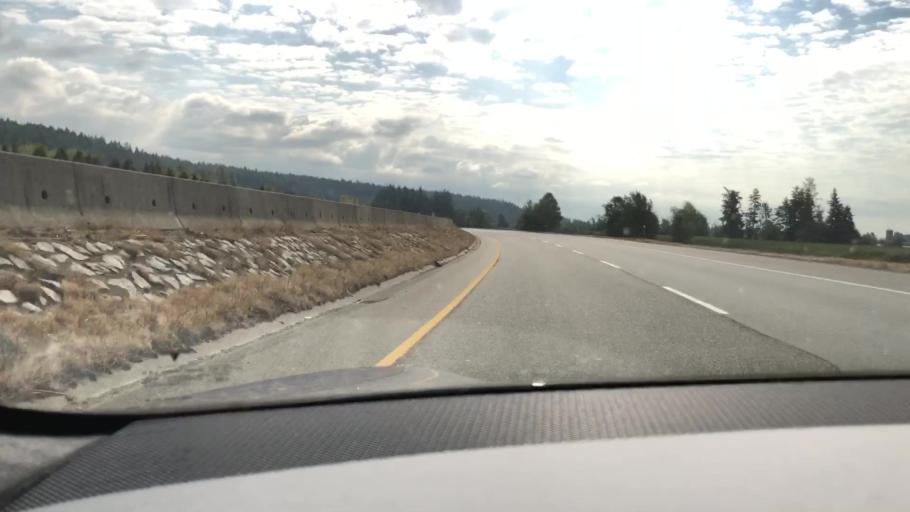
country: CA
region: British Columbia
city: Delta
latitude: 49.1158
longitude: -122.9226
